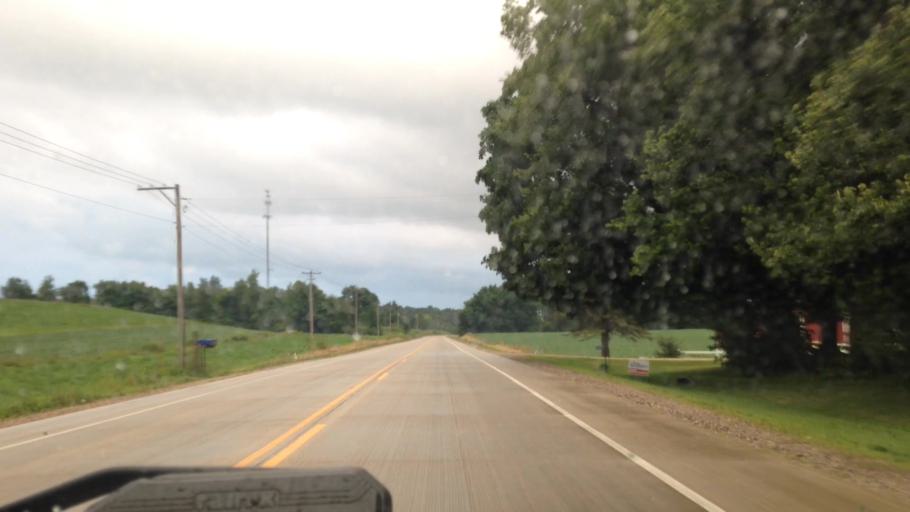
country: US
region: Wisconsin
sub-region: Dodge County
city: Mayville
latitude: 43.4503
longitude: -88.5621
